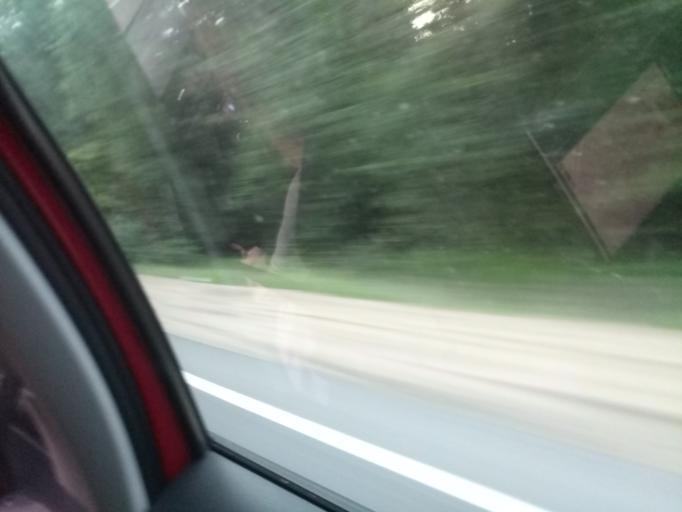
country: RU
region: Moskovskaya
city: Noginsk-9
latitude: 56.0723
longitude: 38.5656
